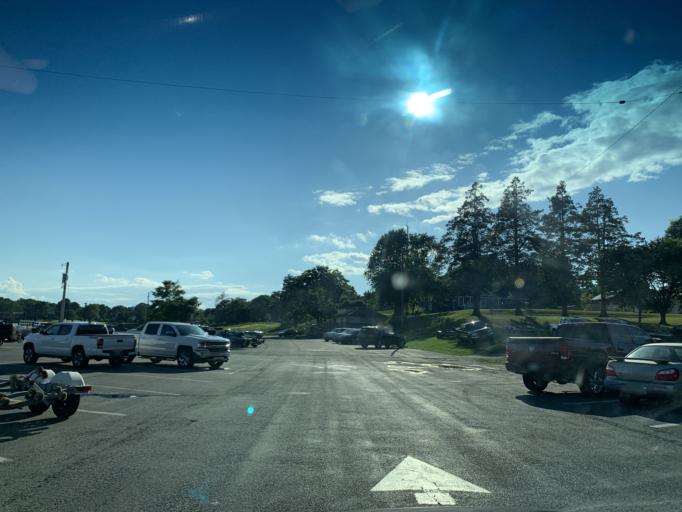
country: US
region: Maryland
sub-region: Harford County
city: Havre de Grace
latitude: 39.5381
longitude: -76.0909
